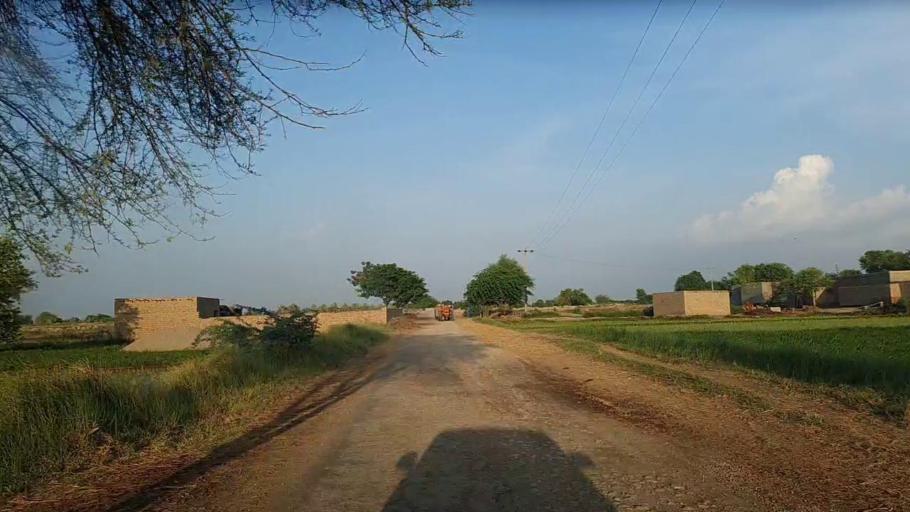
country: PK
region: Sindh
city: Karaundi
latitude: 27.0426
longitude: 68.4110
